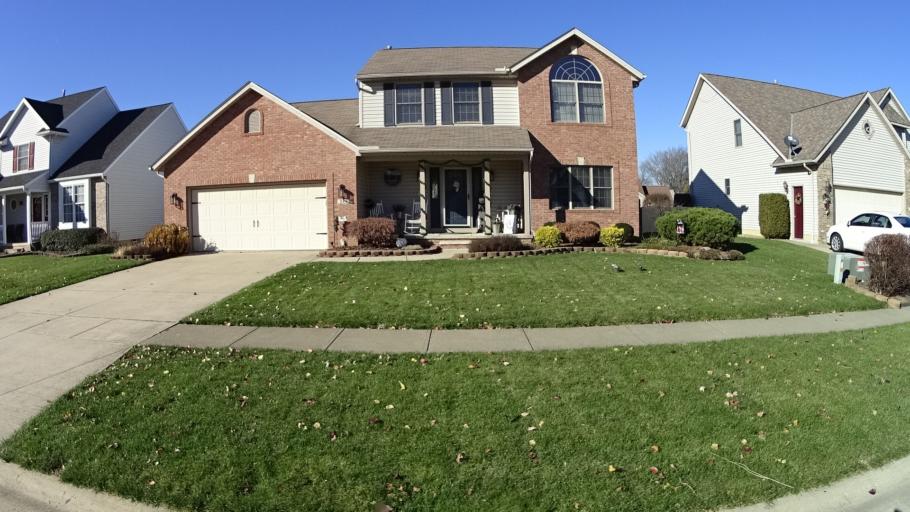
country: US
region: Ohio
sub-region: Lorain County
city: Elyria
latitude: 41.3411
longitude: -82.0847
